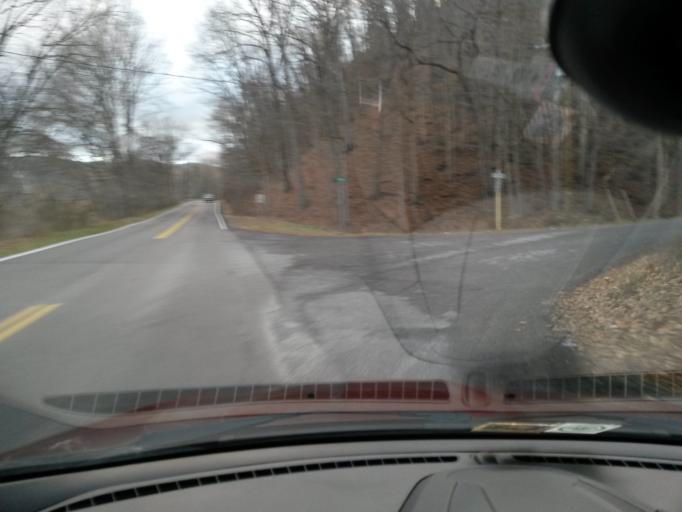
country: US
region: Virginia
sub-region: City of Covington
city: Fairlawn
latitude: 37.7689
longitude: -79.9928
